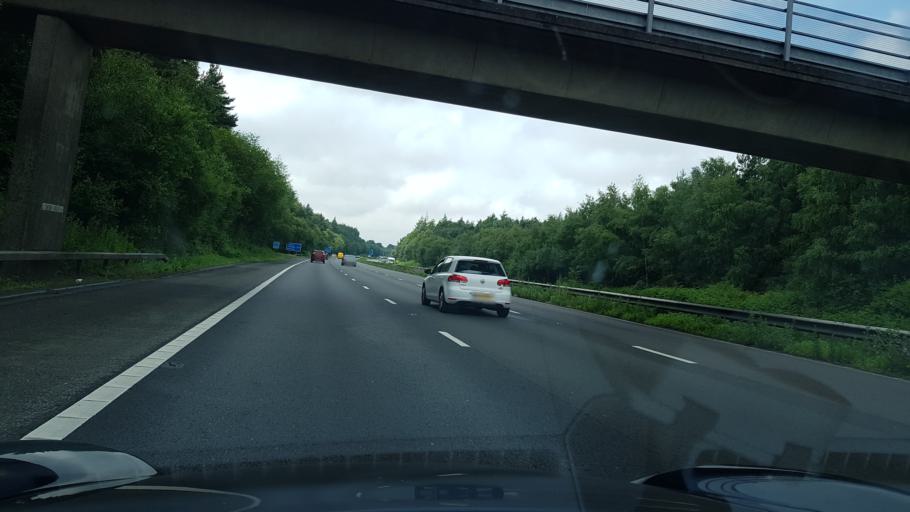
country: GB
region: England
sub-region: West Sussex
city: Furnace Green
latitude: 51.0894
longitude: -0.1764
